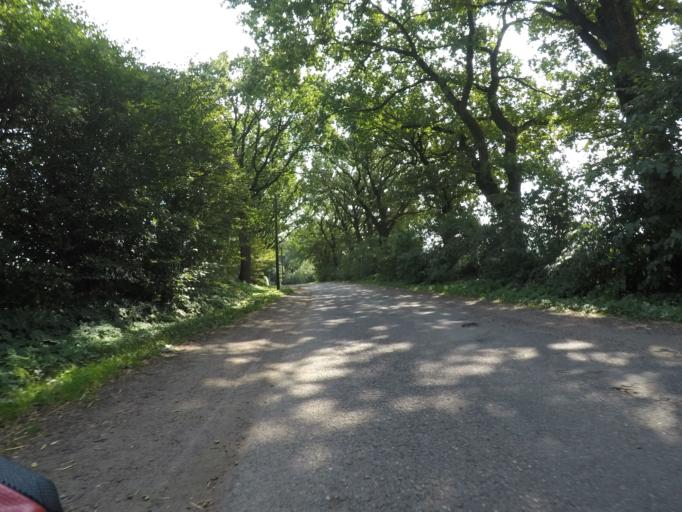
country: DE
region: Schleswig-Holstein
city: Kisdorf
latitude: 53.7994
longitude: 10.0161
